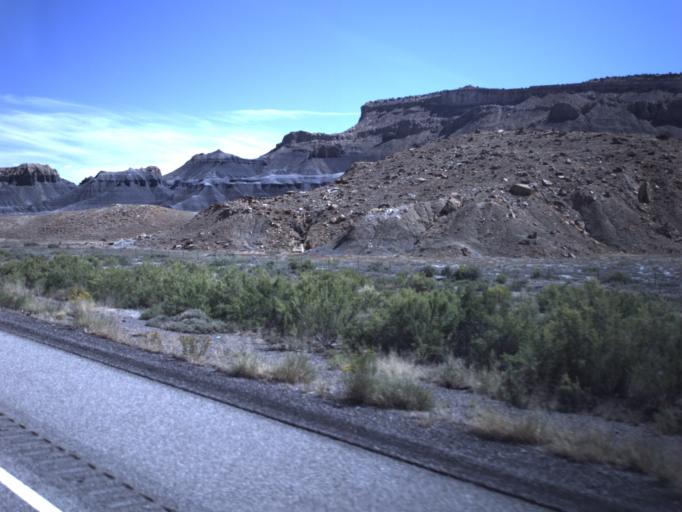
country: US
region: Utah
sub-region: Emery County
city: Ferron
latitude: 38.8095
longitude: -111.2319
